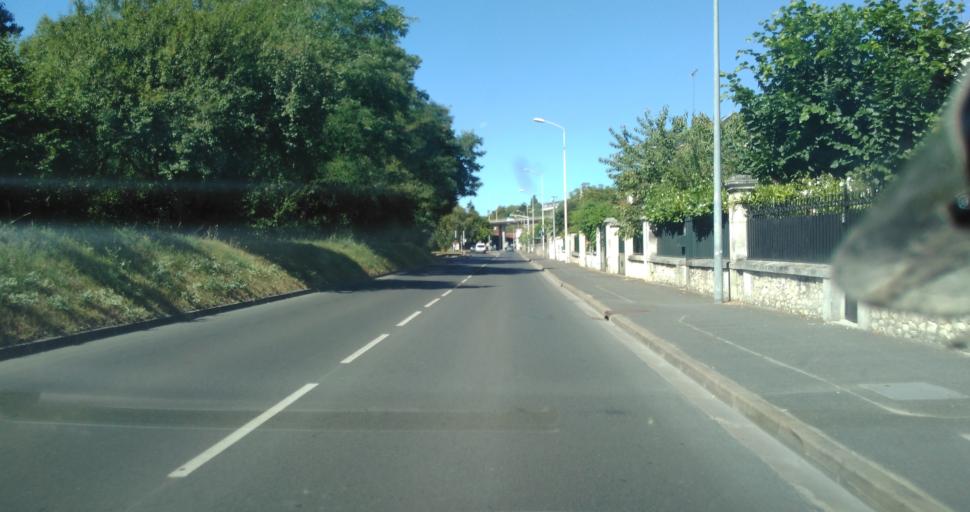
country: FR
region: Centre
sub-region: Departement d'Indre-et-Loire
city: Tours
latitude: 47.4030
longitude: 0.7070
